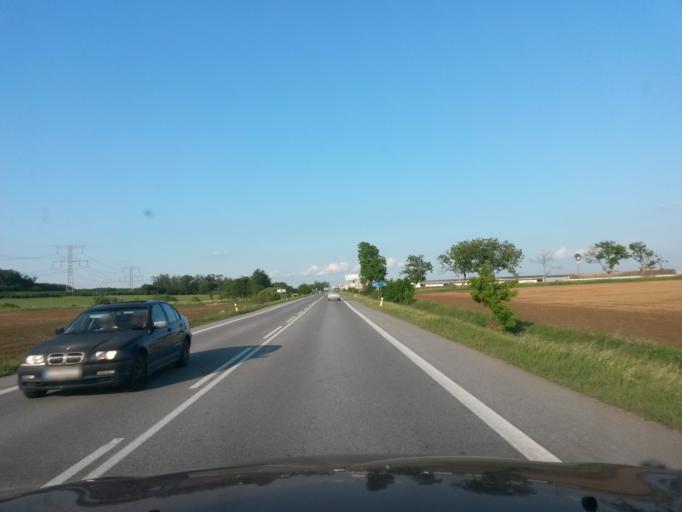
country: SK
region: Kosicky
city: Moldava nad Bodvou
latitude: 48.6053
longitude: 21.1045
